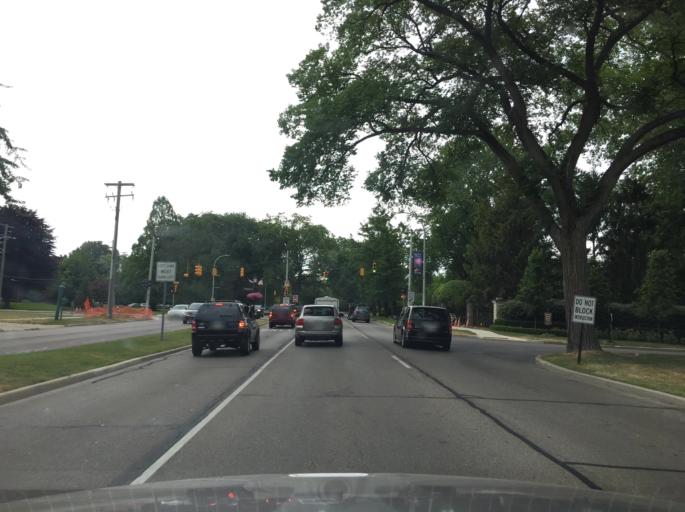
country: US
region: Michigan
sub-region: Wayne County
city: Grosse Pointe Shores
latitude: 42.4355
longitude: -82.8760
